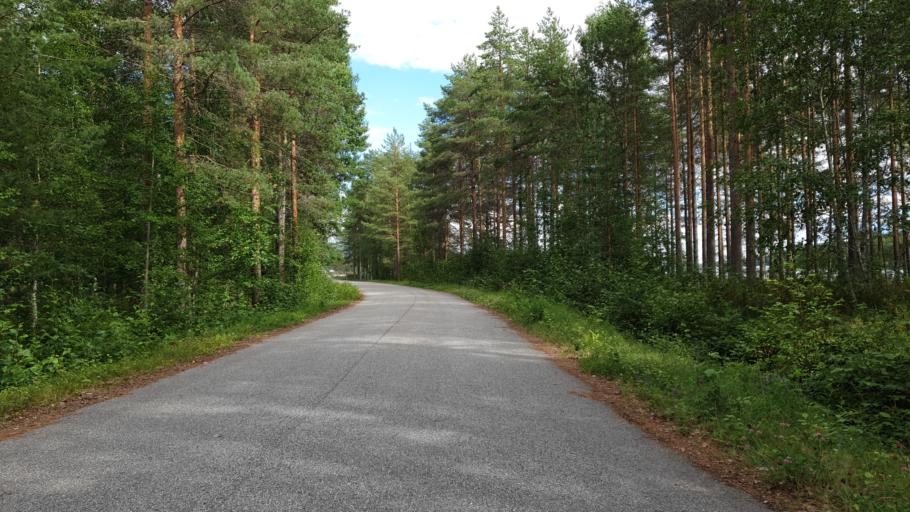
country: FI
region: Kainuu
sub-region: Kehys-Kainuu
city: Kuhmo
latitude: 64.1314
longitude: 29.5457
